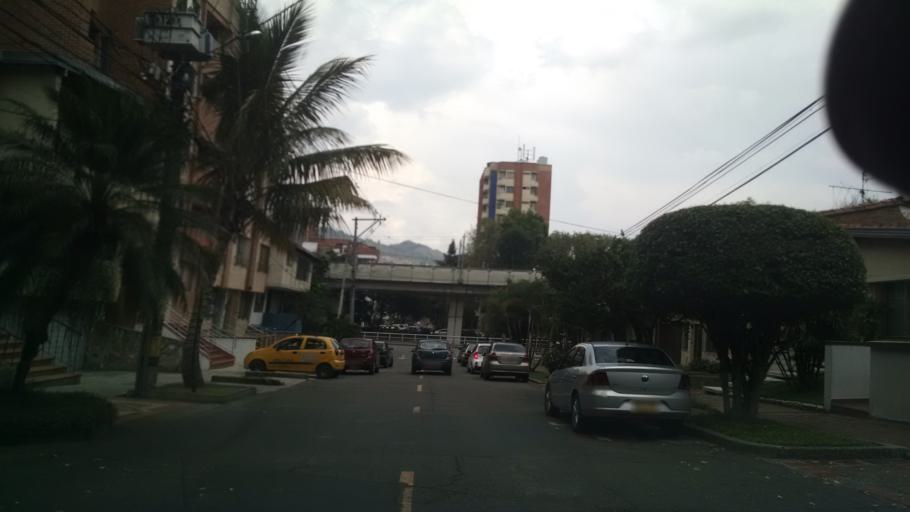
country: CO
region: Antioquia
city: Medellin
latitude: 6.2576
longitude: -75.5971
